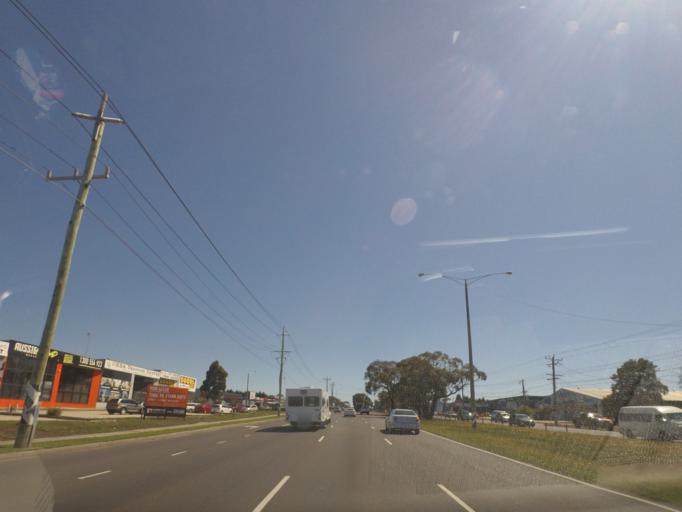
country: AU
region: Victoria
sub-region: Hume
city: Campbellfield
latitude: -37.6807
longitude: 144.9567
